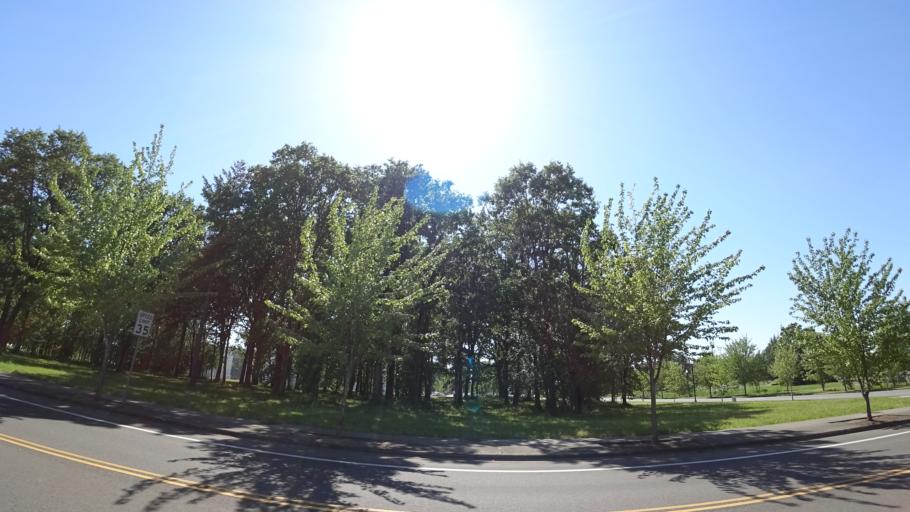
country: US
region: Oregon
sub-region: Washington County
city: Beaverton
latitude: 45.4978
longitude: -122.8134
